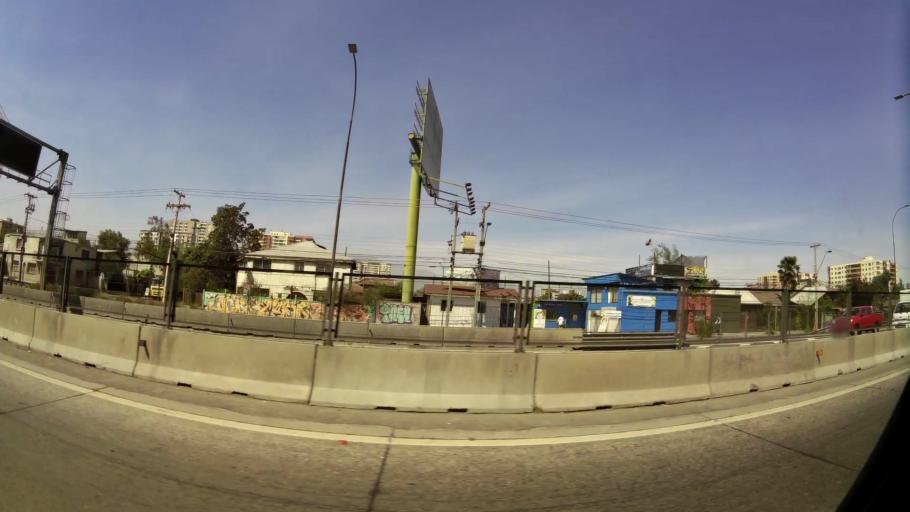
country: CL
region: Santiago Metropolitan
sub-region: Provincia de Santiago
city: Santiago
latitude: -33.4917
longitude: -70.6621
